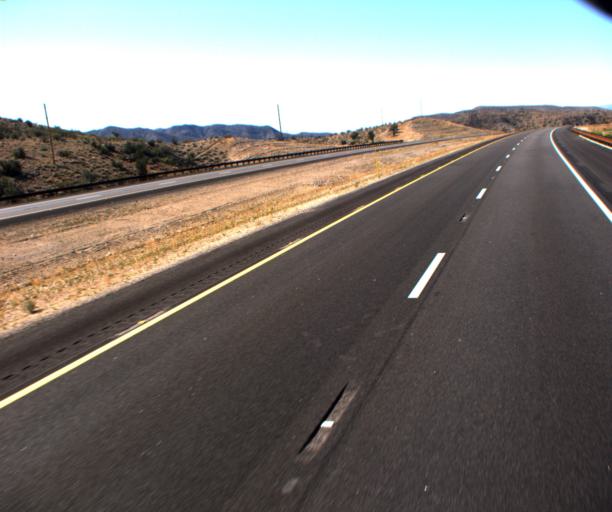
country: US
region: Arizona
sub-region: Mohave County
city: Kingman
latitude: 35.0008
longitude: -113.6644
